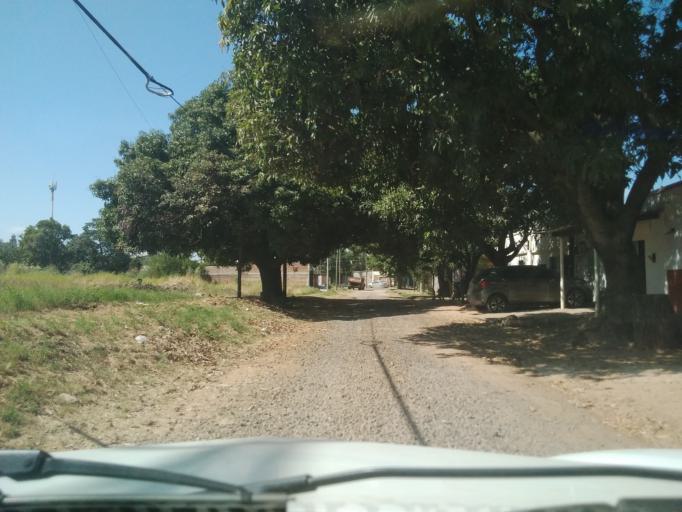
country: AR
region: Corrientes
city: Corrientes
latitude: -27.5051
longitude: -58.8090
